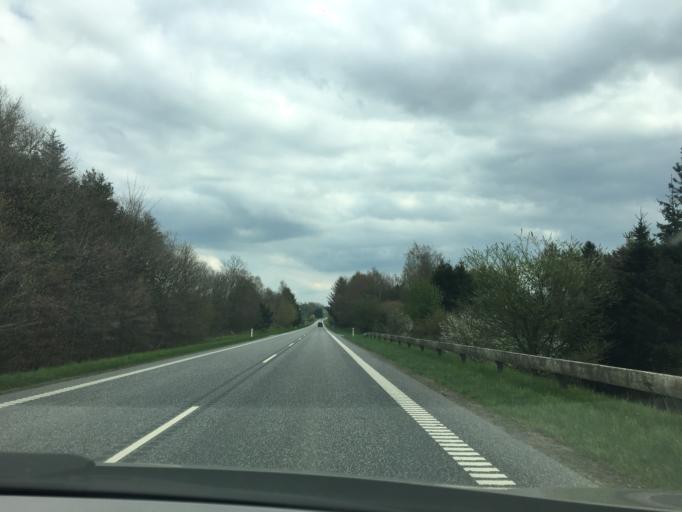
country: DK
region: Central Jutland
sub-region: Horsens Kommune
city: Braedstrup
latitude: 55.9413
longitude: 9.6507
